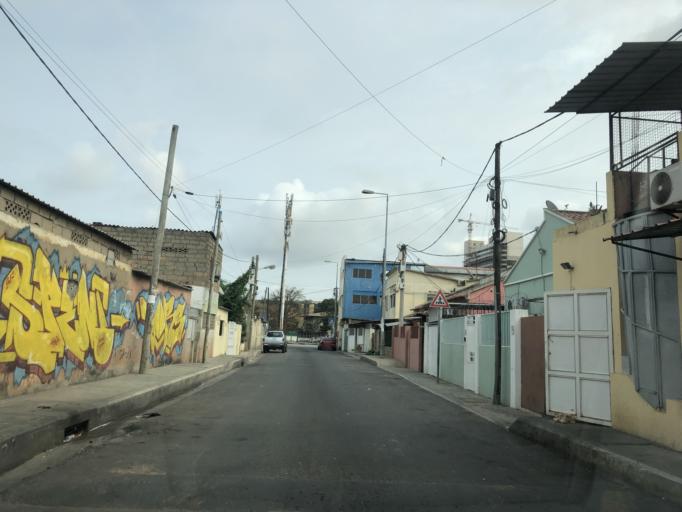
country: AO
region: Luanda
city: Luanda
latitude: -8.8399
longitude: 13.2345
